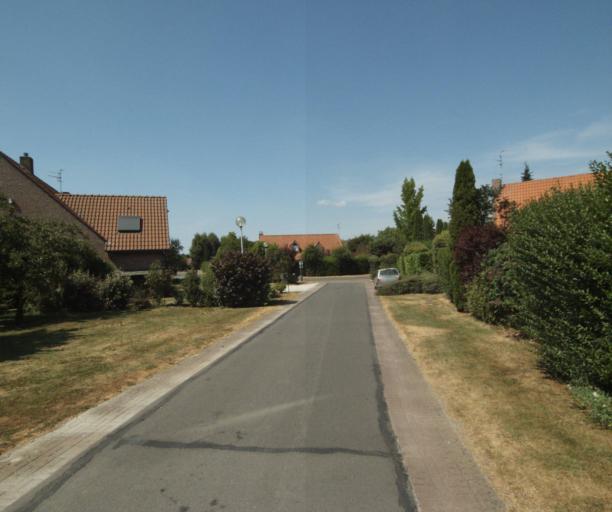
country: FR
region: Nord-Pas-de-Calais
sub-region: Departement du Nord
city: Bondues
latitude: 50.7099
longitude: 3.0869
